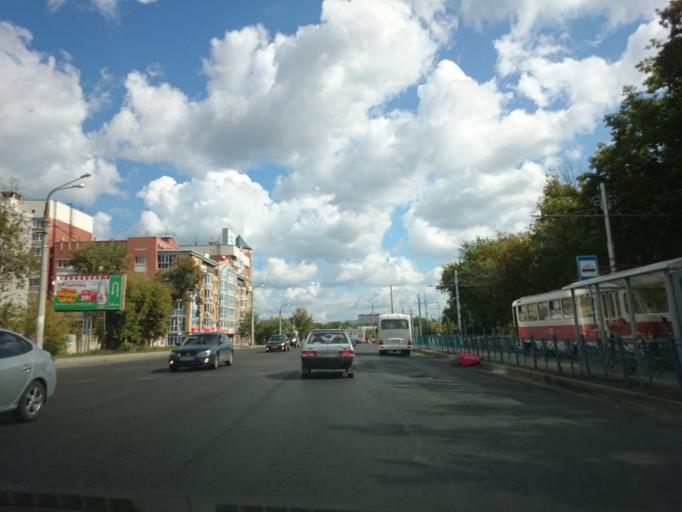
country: RU
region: Samara
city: Samara
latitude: 53.2191
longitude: 50.1545
